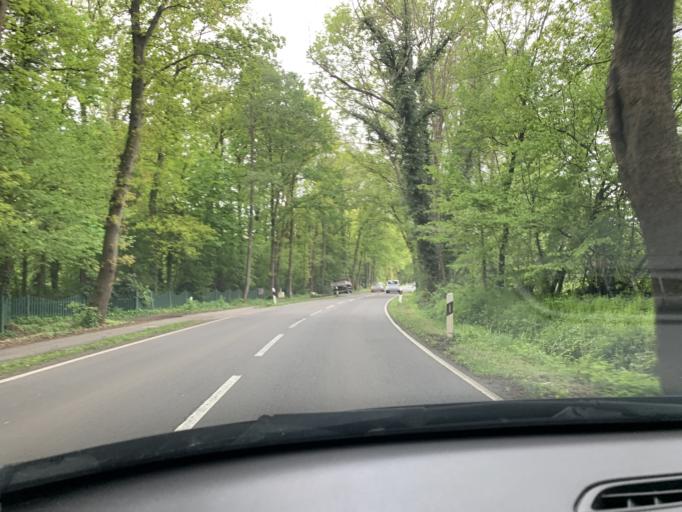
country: DE
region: Lower Saxony
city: Bad Zwischenahn
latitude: 53.2070
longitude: 8.0361
